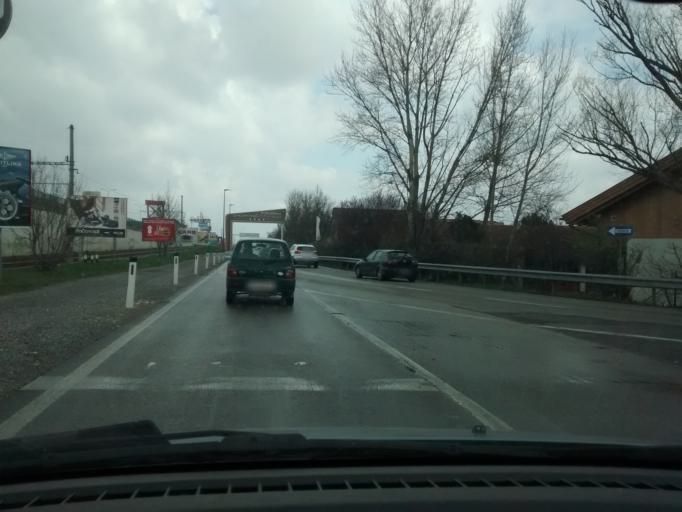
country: AT
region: Lower Austria
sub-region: Politischer Bezirk Modling
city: Wiener Neudorf
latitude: 48.1004
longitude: 16.3153
